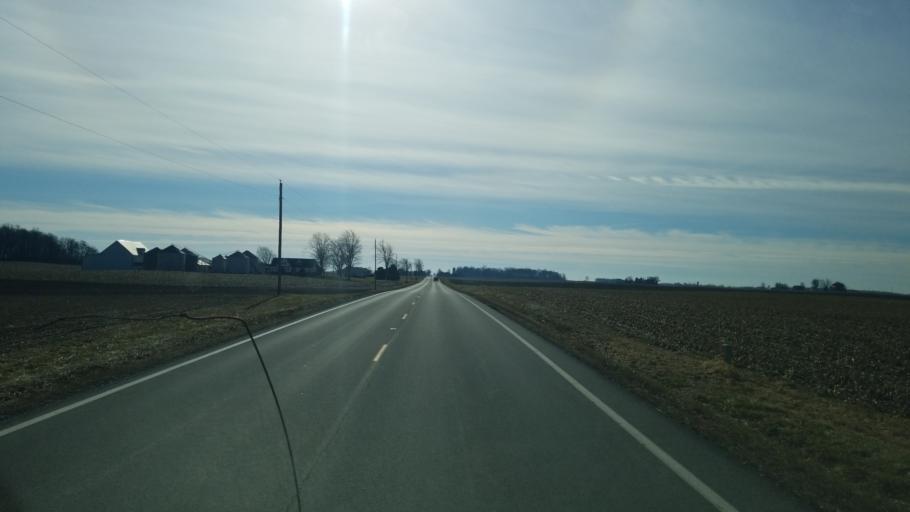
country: US
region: Ohio
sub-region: Putnam County
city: Leipsic
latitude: 41.0782
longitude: -83.9865
